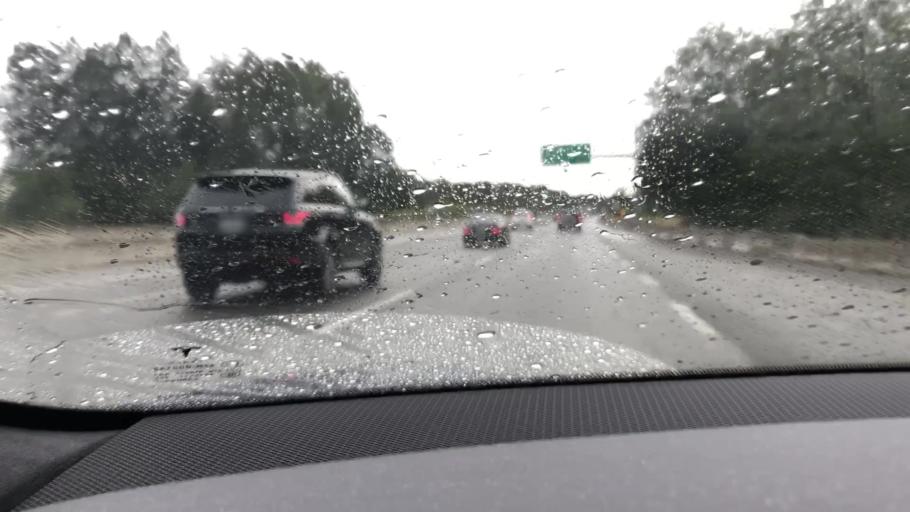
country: CA
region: British Columbia
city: Burnaby
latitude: 49.2417
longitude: -122.9635
